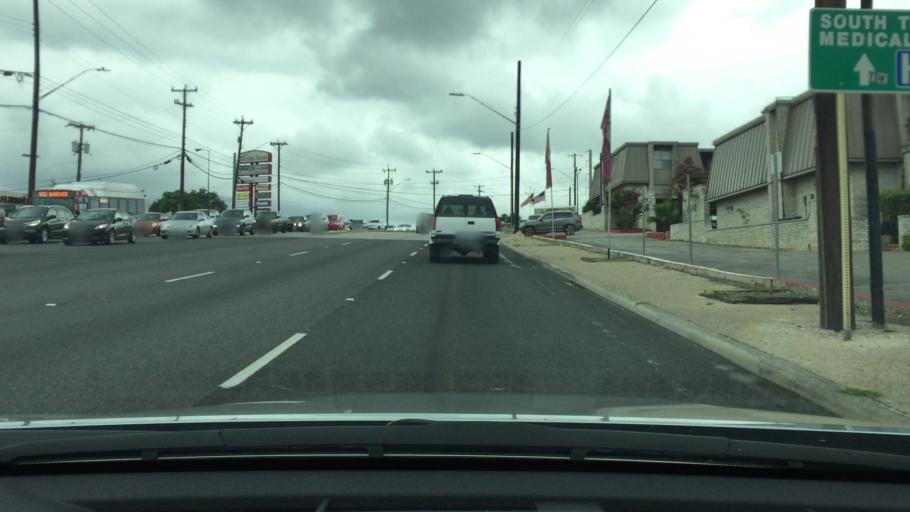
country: US
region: Texas
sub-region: Bexar County
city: Balcones Heights
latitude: 29.4910
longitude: -98.5688
